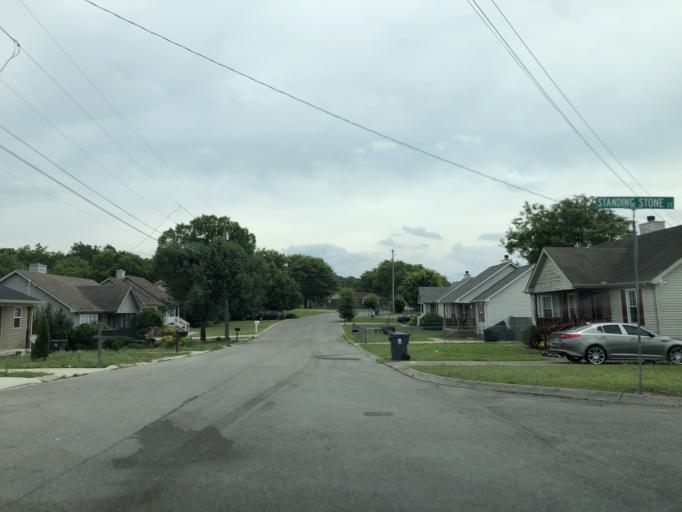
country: US
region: Tennessee
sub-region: Davidson County
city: Nashville
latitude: 36.2482
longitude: -86.7754
